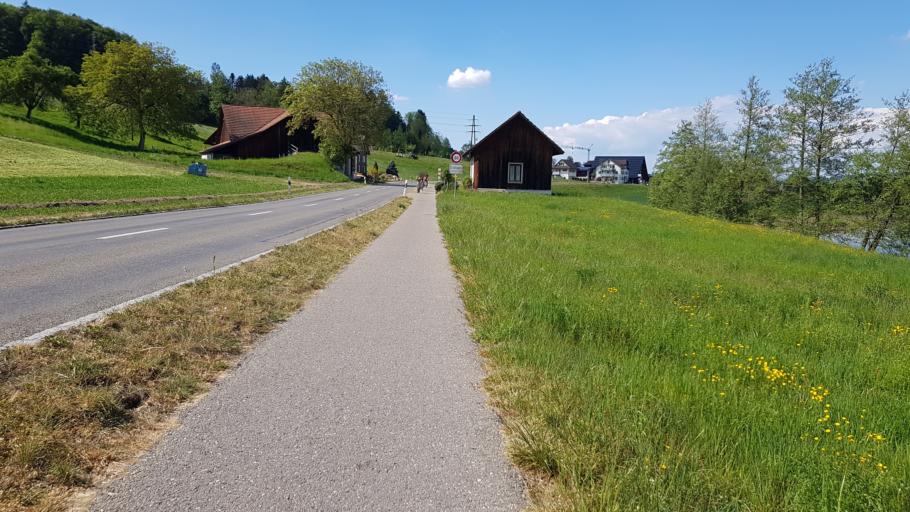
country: CH
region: Lucerne
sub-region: Hochdorf District
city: Hitzkirch
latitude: 47.2071
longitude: 8.2436
